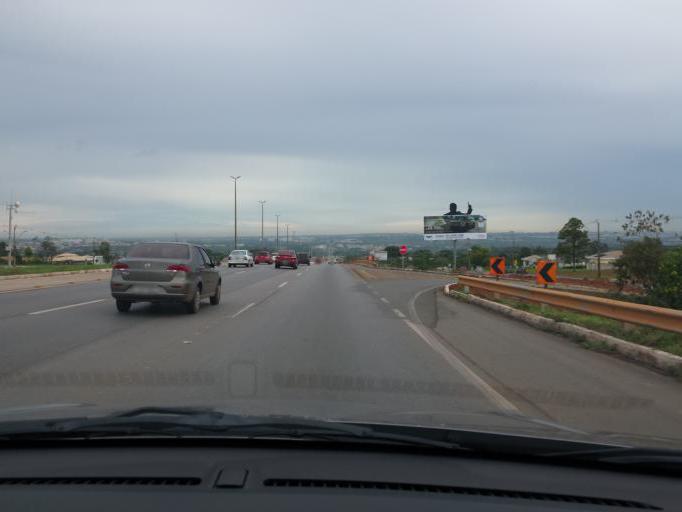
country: BR
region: Federal District
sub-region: Brasilia
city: Brasilia
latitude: -15.8988
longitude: -47.9625
